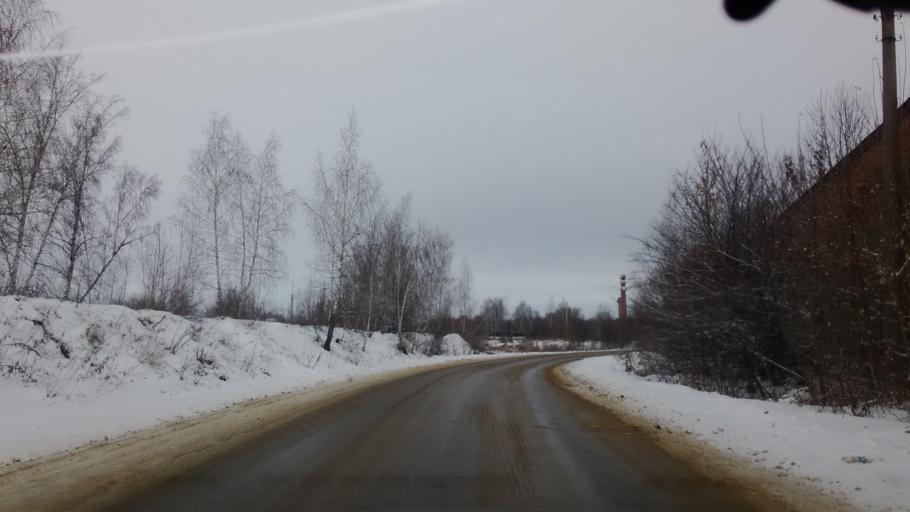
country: RU
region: Tula
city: Bogoroditsk
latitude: 53.7613
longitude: 38.1055
